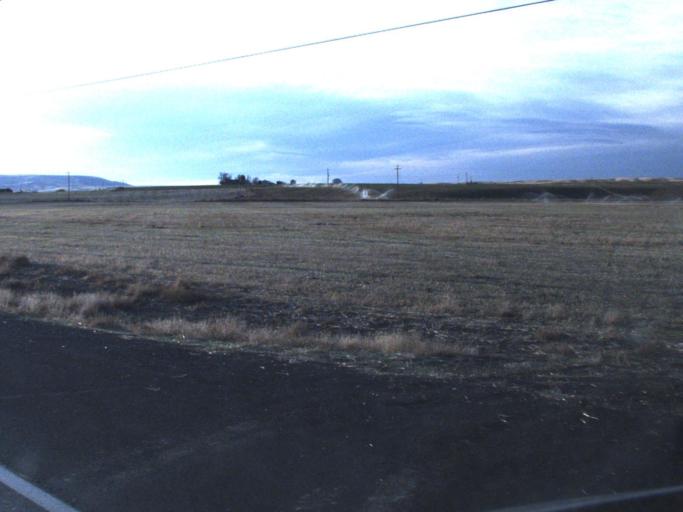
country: US
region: Washington
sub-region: Walla Walla County
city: Garrett
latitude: 46.0463
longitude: -118.6384
